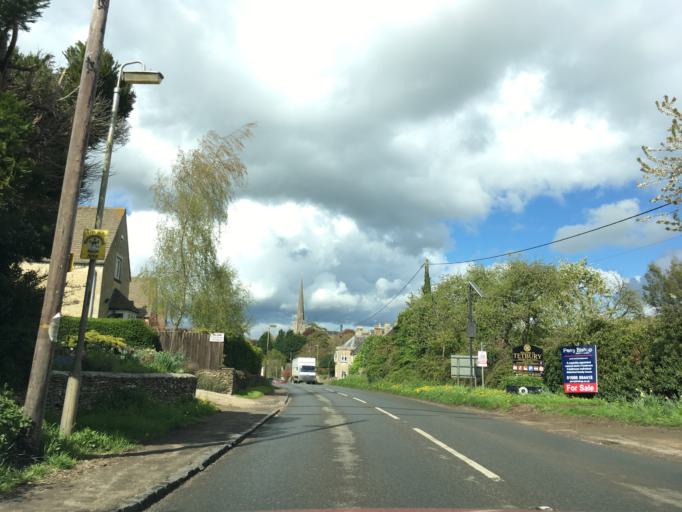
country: GB
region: England
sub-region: Gloucestershire
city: Tetbury
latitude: 51.6322
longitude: -2.1635
